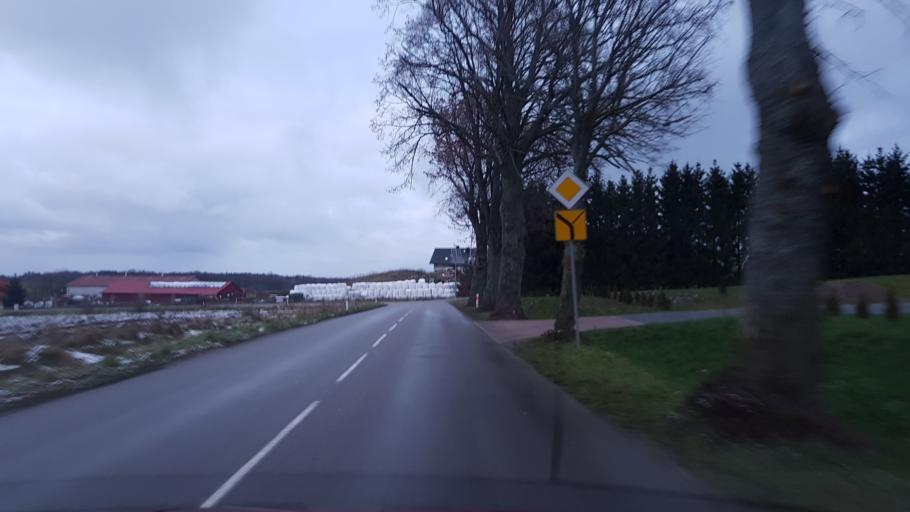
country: PL
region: Pomeranian Voivodeship
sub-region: Powiat bytowski
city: Tuchomie
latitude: 54.1220
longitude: 17.3382
